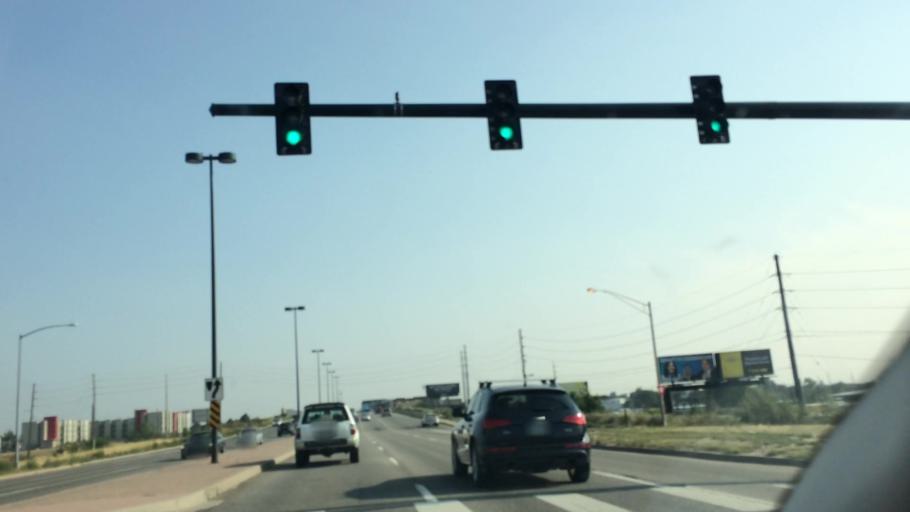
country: US
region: Colorado
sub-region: Adams County
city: Commerce City
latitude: 39.7790
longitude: -104.9406
